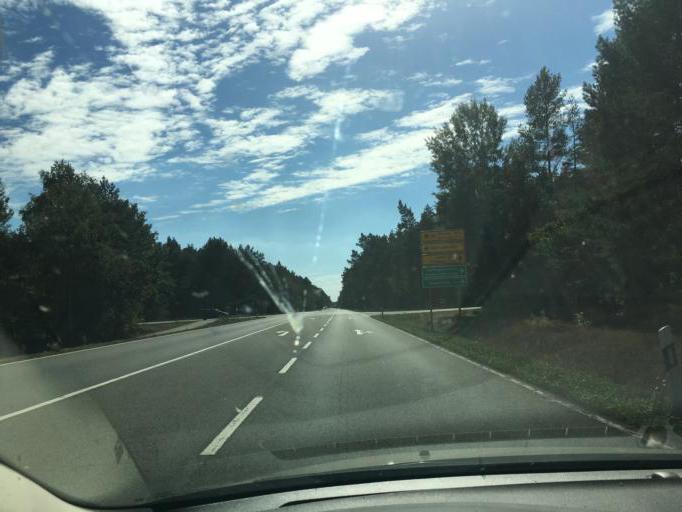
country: DE
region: Saxony-Anhalt
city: Seehausen
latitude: 52.8616
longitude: 11.7316
